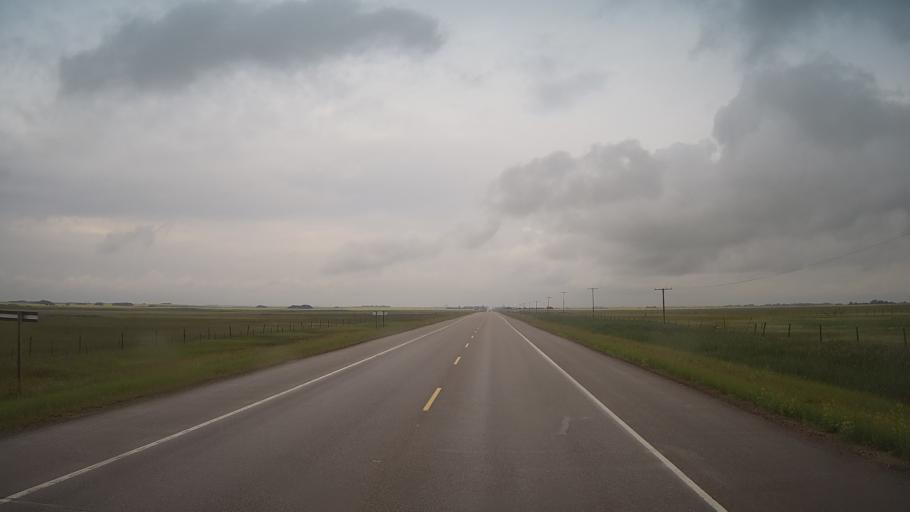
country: CA
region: Saskatchewan
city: Unity
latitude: 52.4349
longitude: -108.9804
